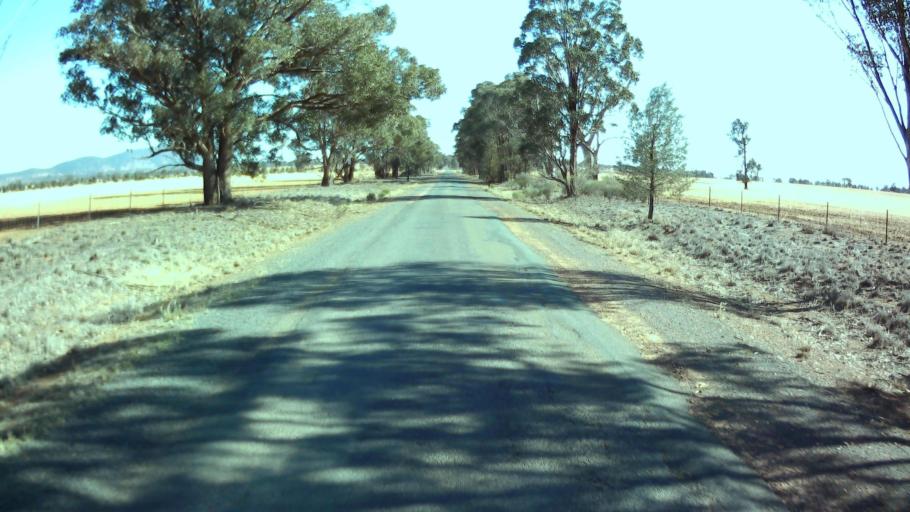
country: AU
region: New South Wales
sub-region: Weddin
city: Grenfell
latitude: -33.8035
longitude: 147.9553
